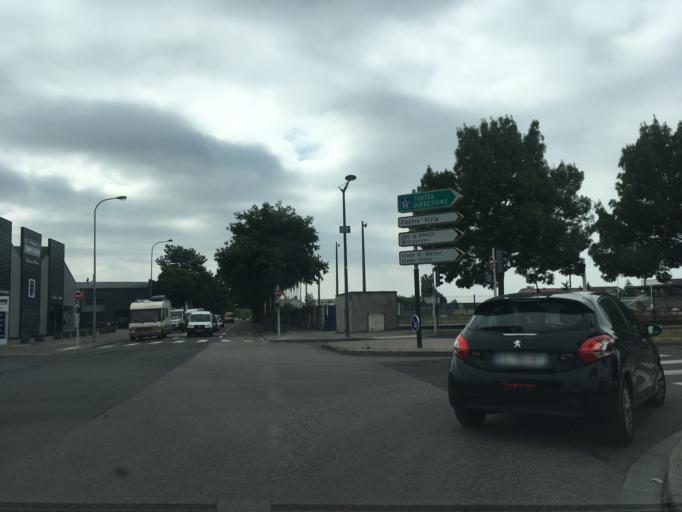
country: FR
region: Lorraine
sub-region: Departement de Meurthe-et-Moselle
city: Tomblaine
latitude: 48.6900
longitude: 6.2027
